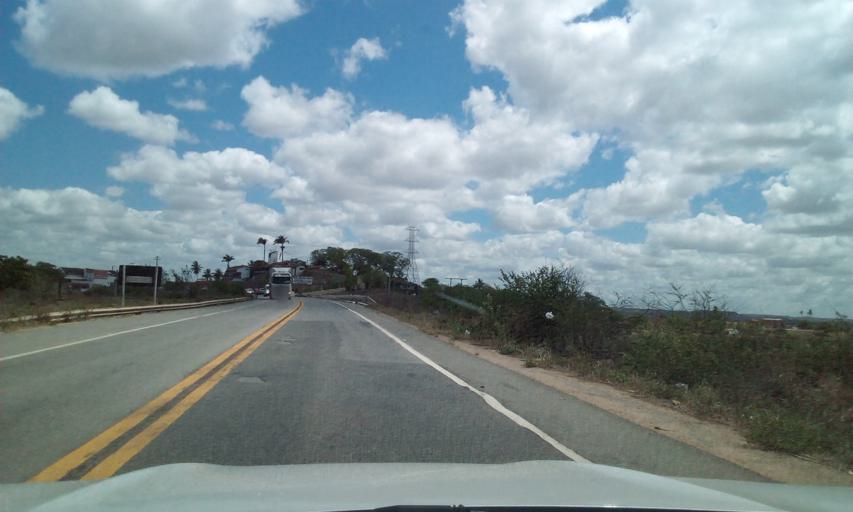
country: BR
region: Sergipe
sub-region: Propria
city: Propria
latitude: -10.2177
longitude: -36.8249
